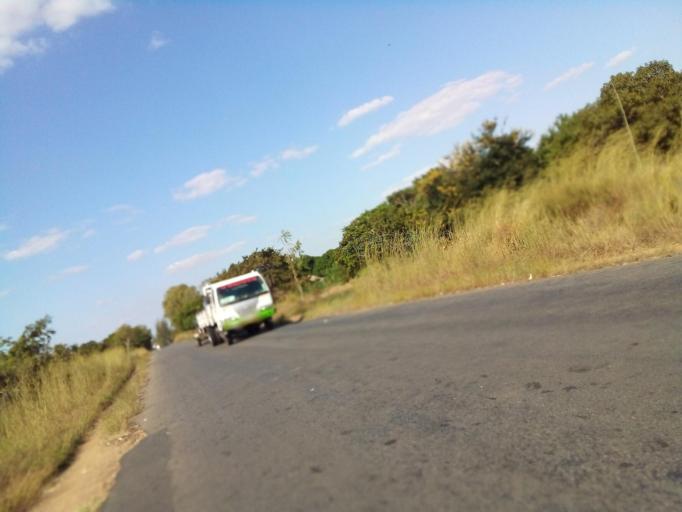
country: MZ
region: Zambezia
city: Quelimane
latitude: -17.5760
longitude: 36.6377
